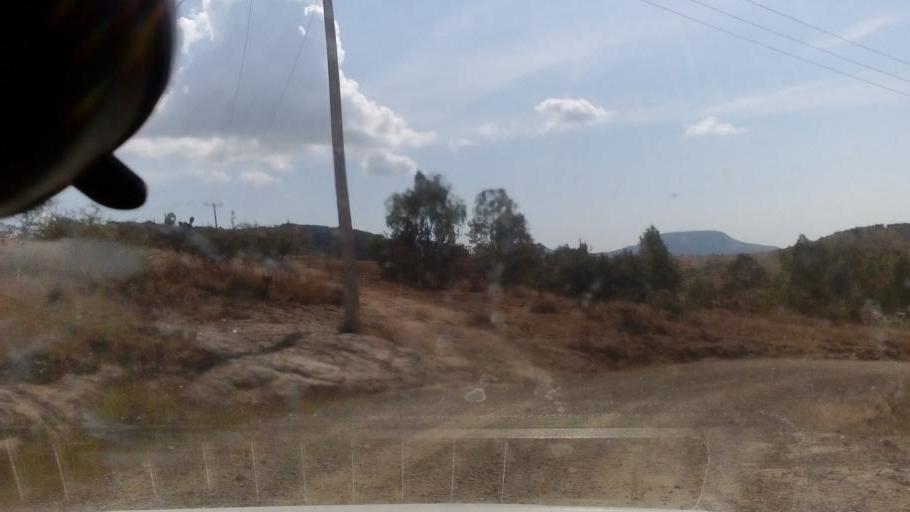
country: MX
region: Guanajuato
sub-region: Leon
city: Lucio Blanco (Los Gavilanes)
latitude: 21.1914
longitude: -101.4968
